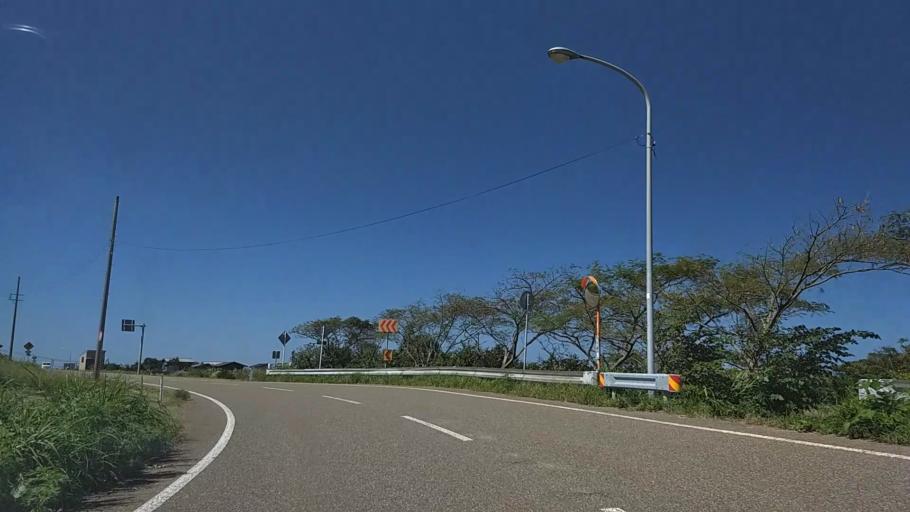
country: JP
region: Niigata
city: Joetsu
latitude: 37.1725
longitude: 138.1019
